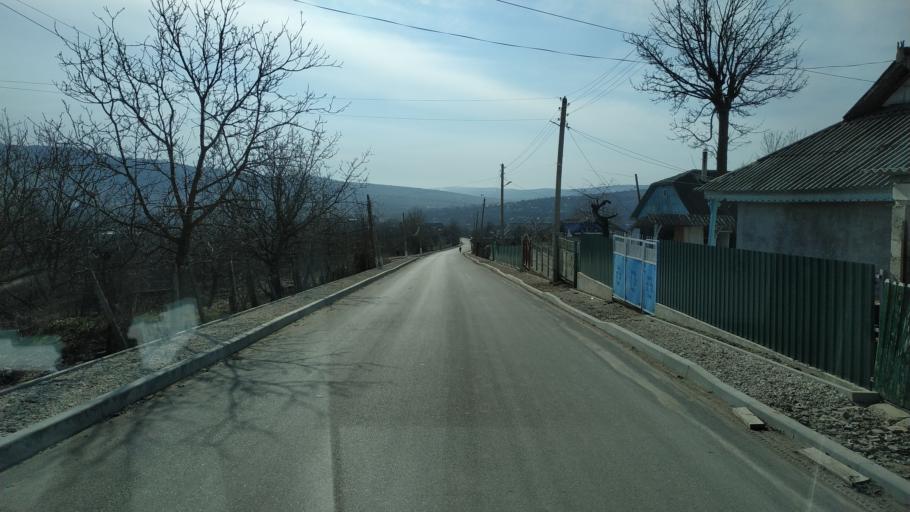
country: MD
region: Nisporeni
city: Nisporeni
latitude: 47.1705
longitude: 28.1308
